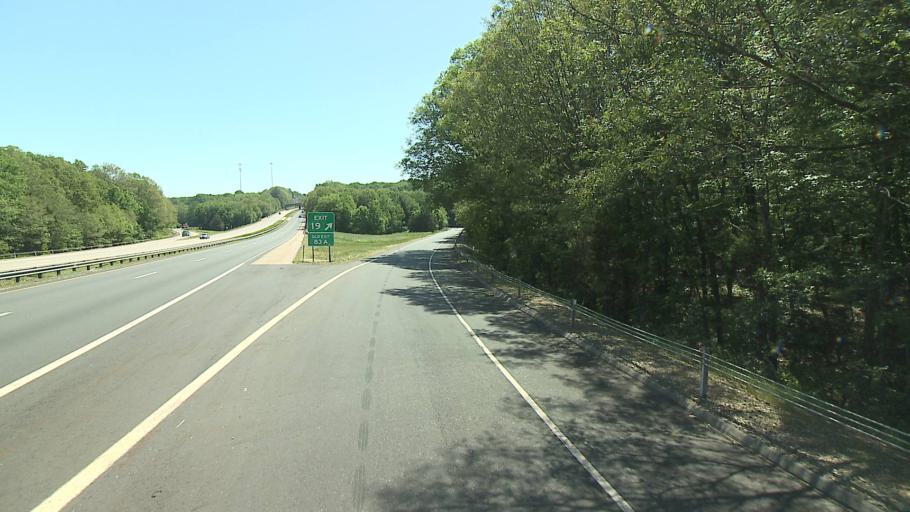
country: US
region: Connecticut
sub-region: New London County
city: Lisbon
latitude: 41.5881
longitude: -72.0257
